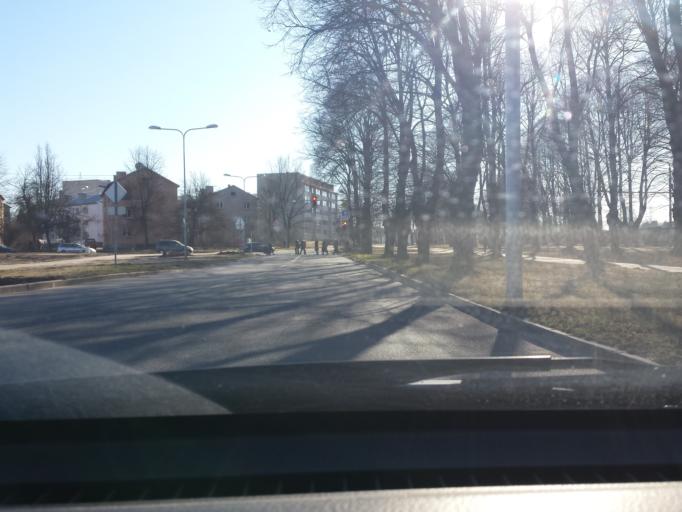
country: LV
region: Riga
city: Jaunciems
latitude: 56.9901
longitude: 24.1656
